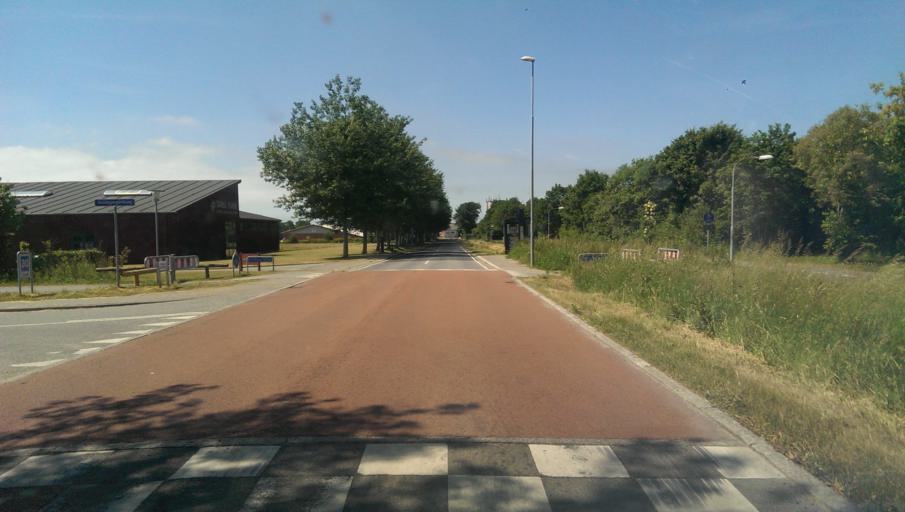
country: DK
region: South Denmark
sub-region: Esbjerg Kommune
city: Esbjerg
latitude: 55.5305
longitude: 8.4090
